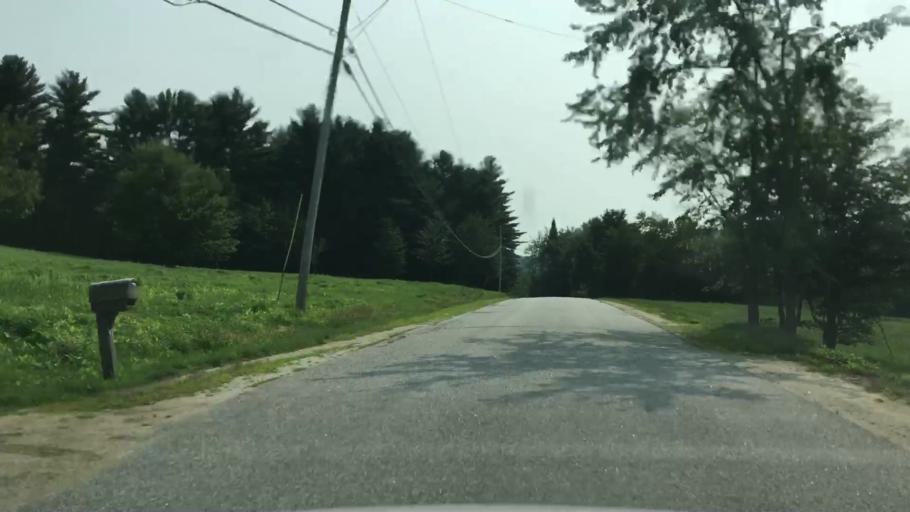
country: US
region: Maine
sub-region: Oxford County
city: Buckfield
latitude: 44.2898
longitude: -70.3455
